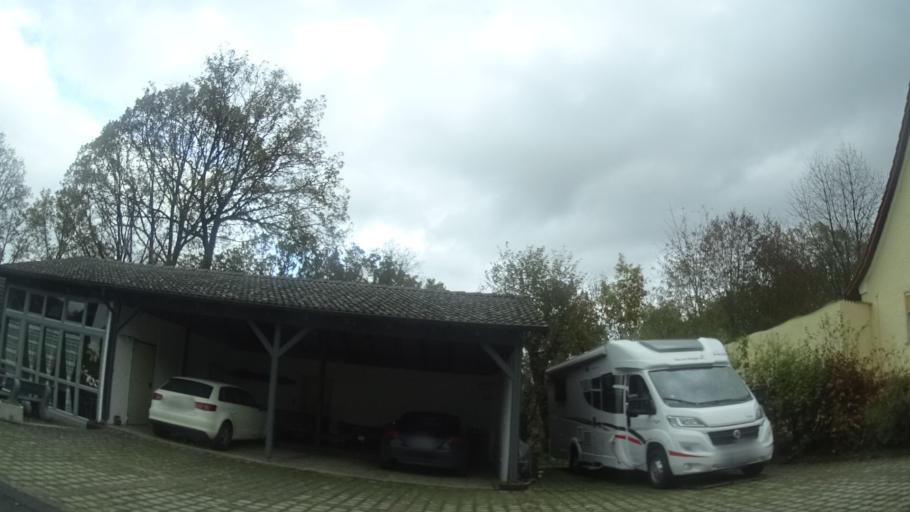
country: DE
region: Bavaria
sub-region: Regierungsbezirk Unterfranken
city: Oberelsbach
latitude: 50.3774
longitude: 10.1044
